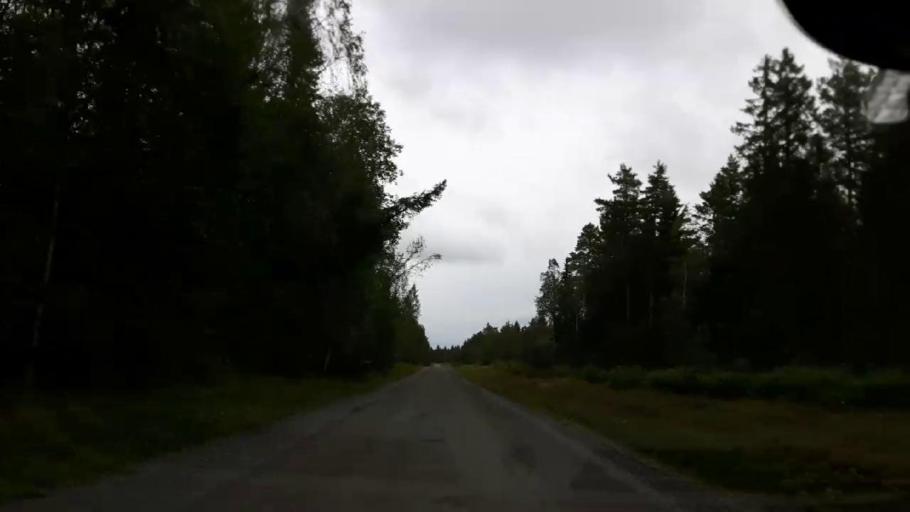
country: SE
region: Jaemtland
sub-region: OEstersunds Kommun
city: Ostersund
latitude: 63.0724
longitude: 14.5533
